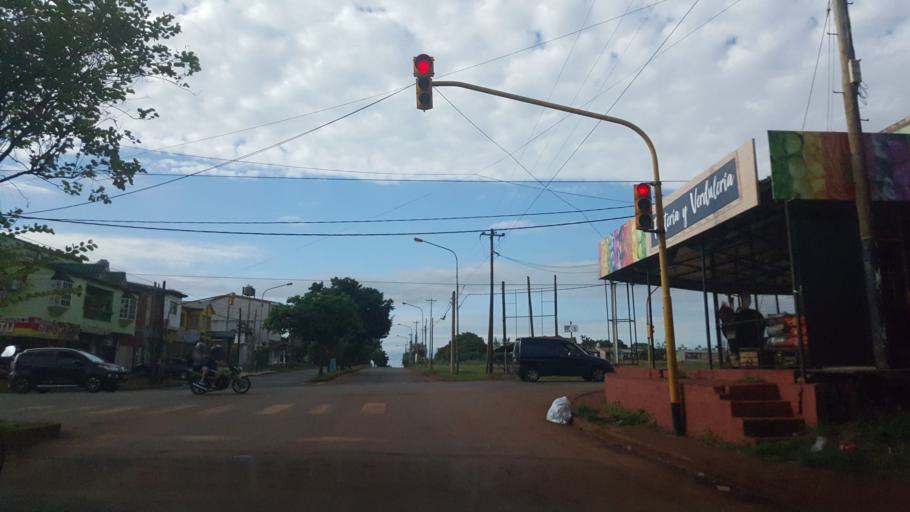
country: AR
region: Misiones
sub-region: Departamento de Capital
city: Posadas
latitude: -27.3876
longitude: -55.9345
